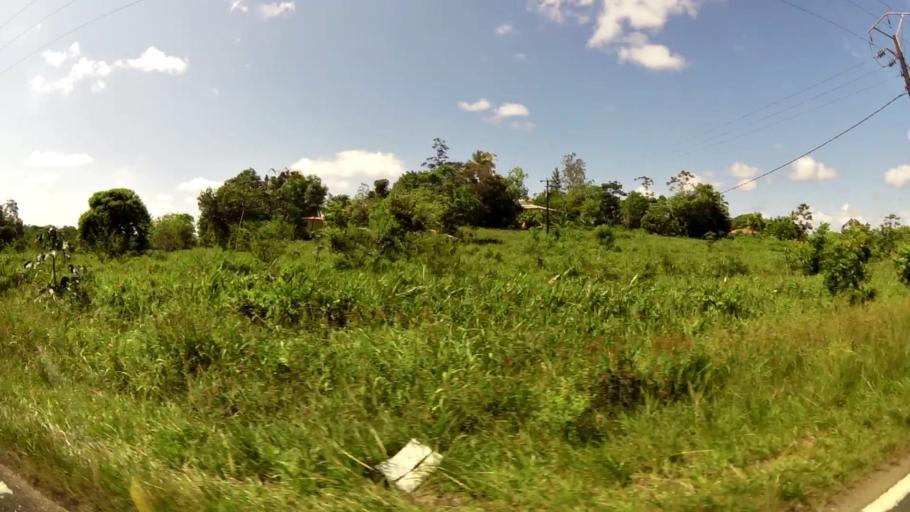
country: GF
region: Guyane
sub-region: Guyane
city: Matoury
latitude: 4.8283
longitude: -52.3570
